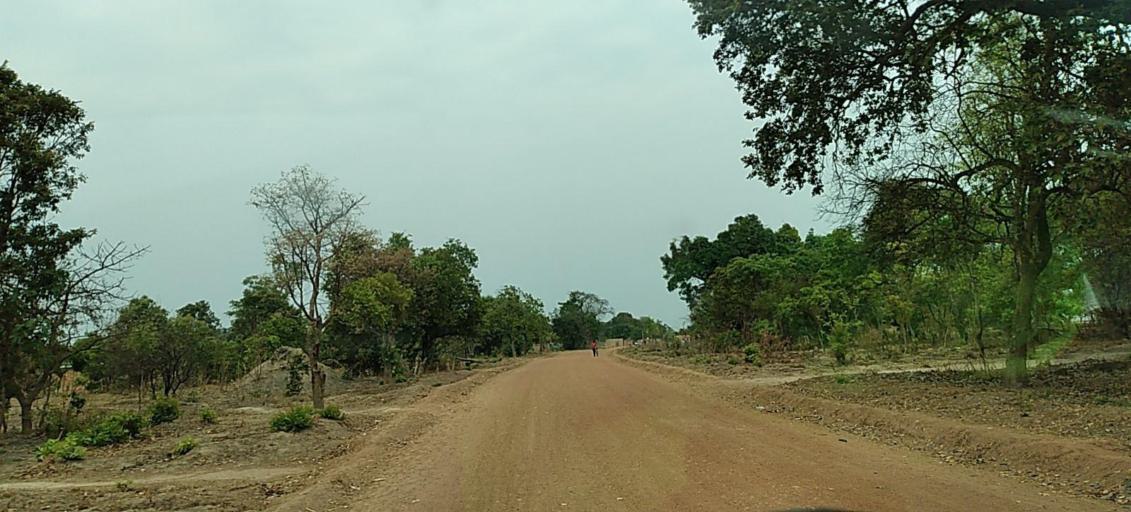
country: ZM
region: North-Western
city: Solwezi
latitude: -12.4756
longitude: 26.5299
